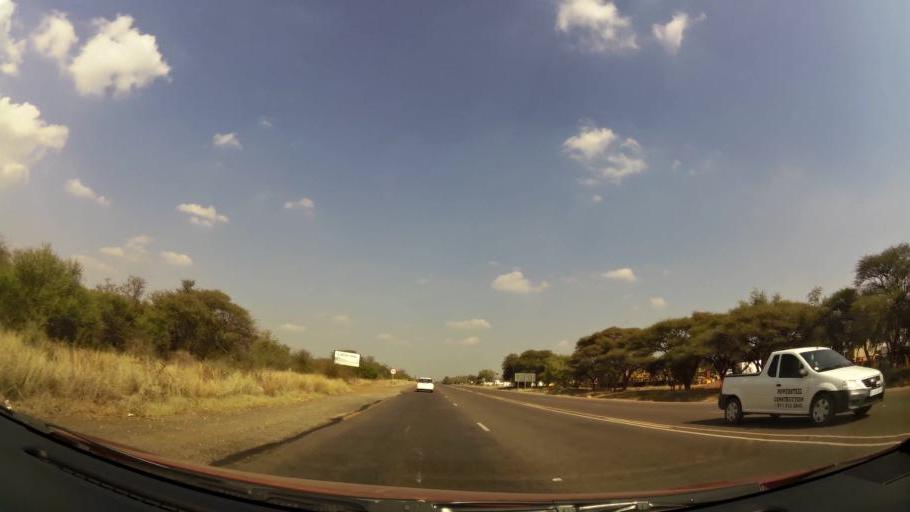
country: ZA
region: North-West
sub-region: Bojanala Platinum District Municipality
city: Mogwase
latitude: -25.4449
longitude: 27.0881
